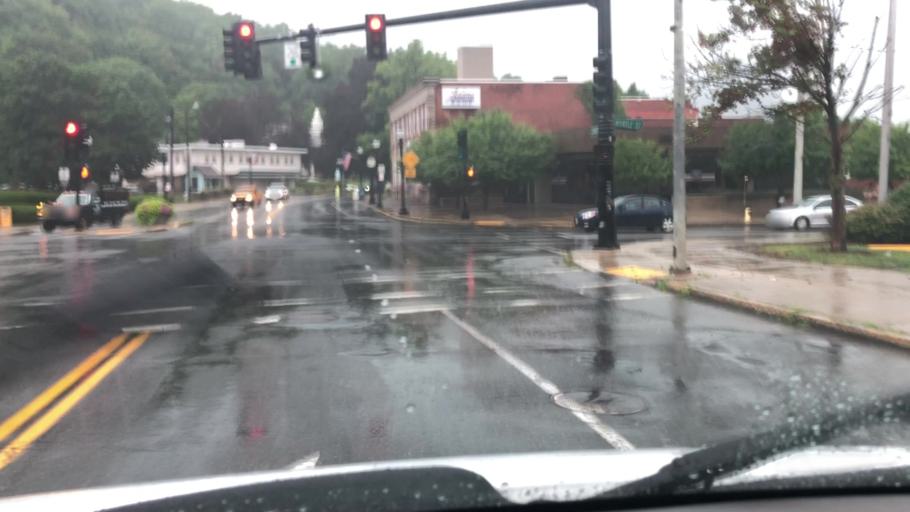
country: US
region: Massachusetts
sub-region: Berkshire County
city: Adams
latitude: 42.6199
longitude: -73.1199
